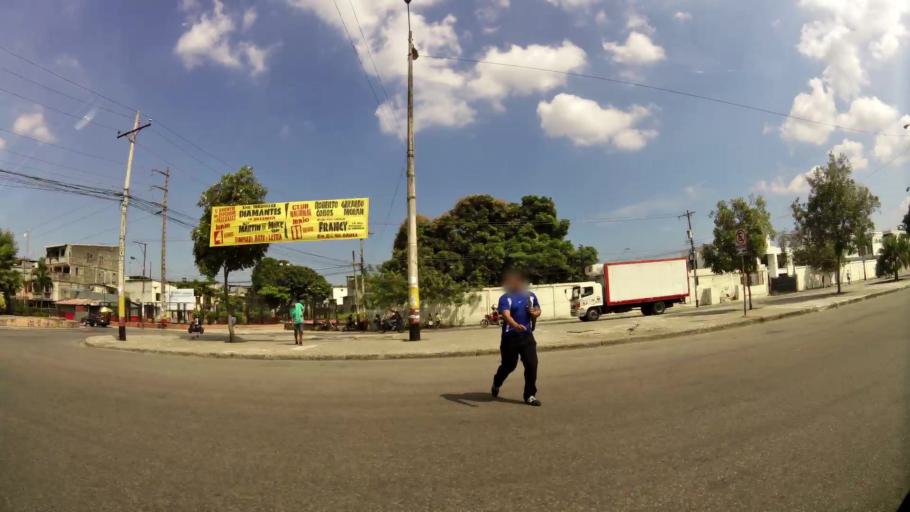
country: EC
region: Guayas
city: Santa Lucia
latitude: -2.1285
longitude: -79.9384
